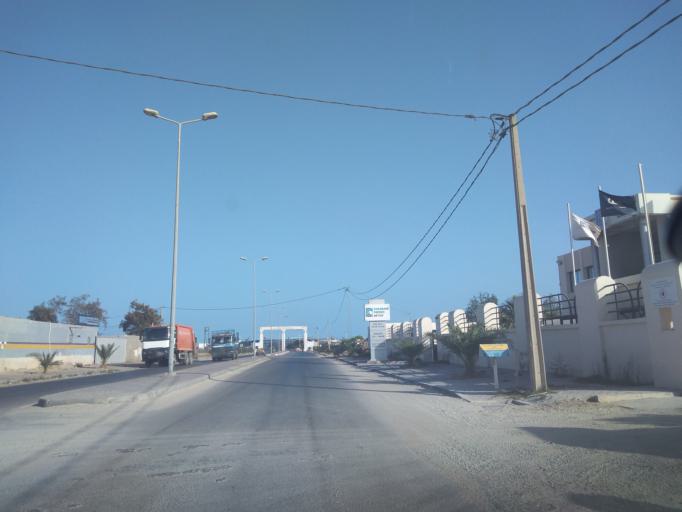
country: TN
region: Safaqis
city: Sfax
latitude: 34.7229
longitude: 10.7590
